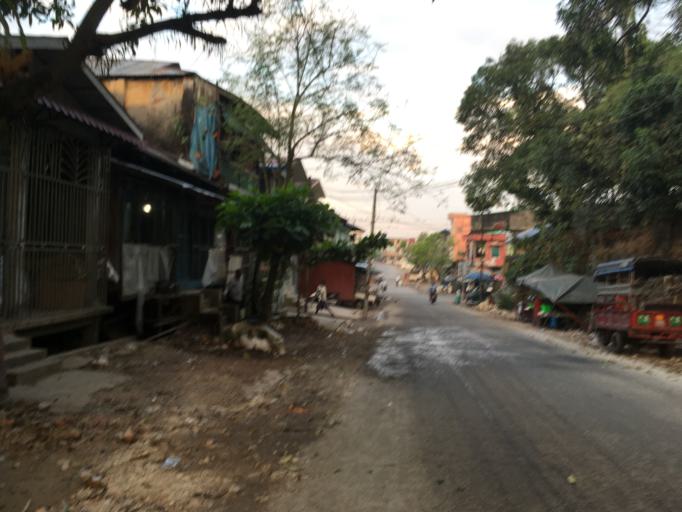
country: MM
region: Mon
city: Mawlamyine
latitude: 16.4856
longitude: 97.6244
